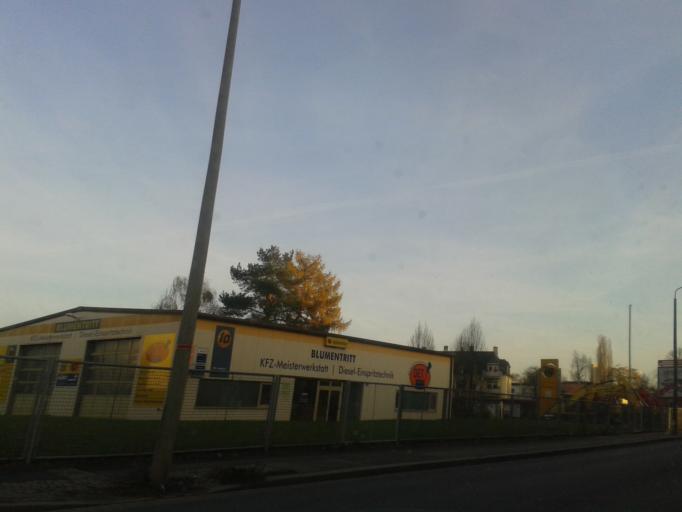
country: DE
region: Saxony
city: Heidenau
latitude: 51.0048
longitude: 13.8228
